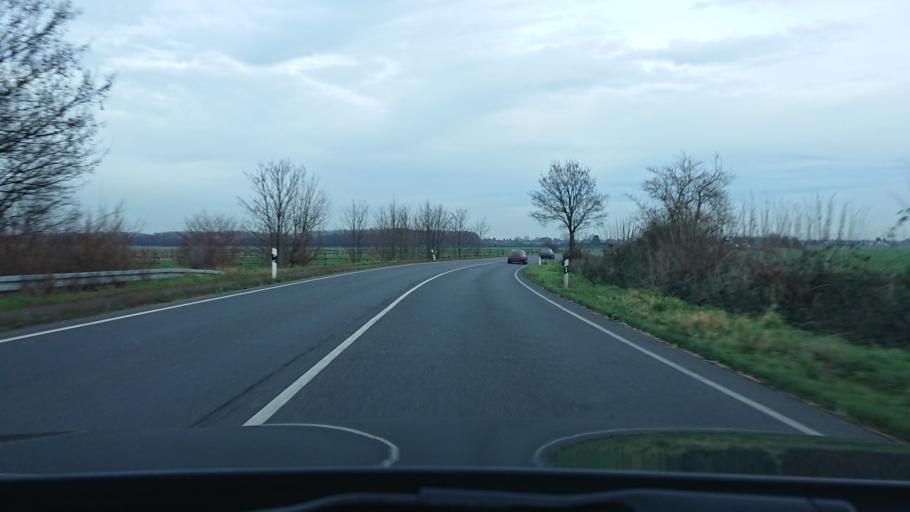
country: DE
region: North Rhine-Westphalia
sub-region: Regierungsbezirk Koln
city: Sinnersdorf
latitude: 51.0232
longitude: 6.7906
